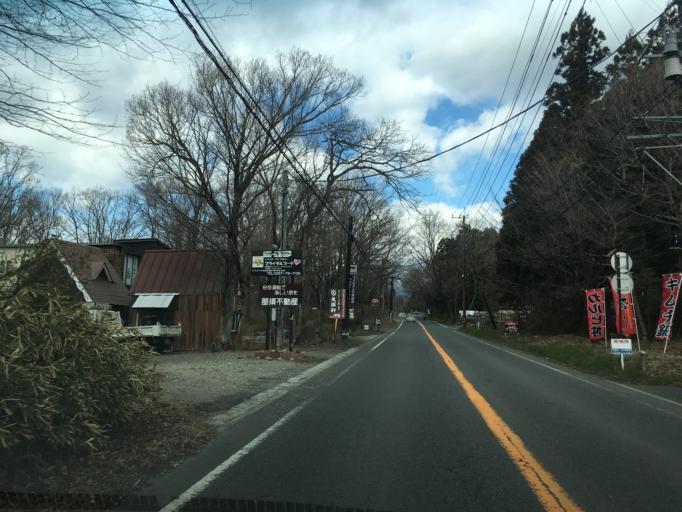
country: JP
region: Tochigi
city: Kuroiso
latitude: 37.0371
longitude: 140.0175
